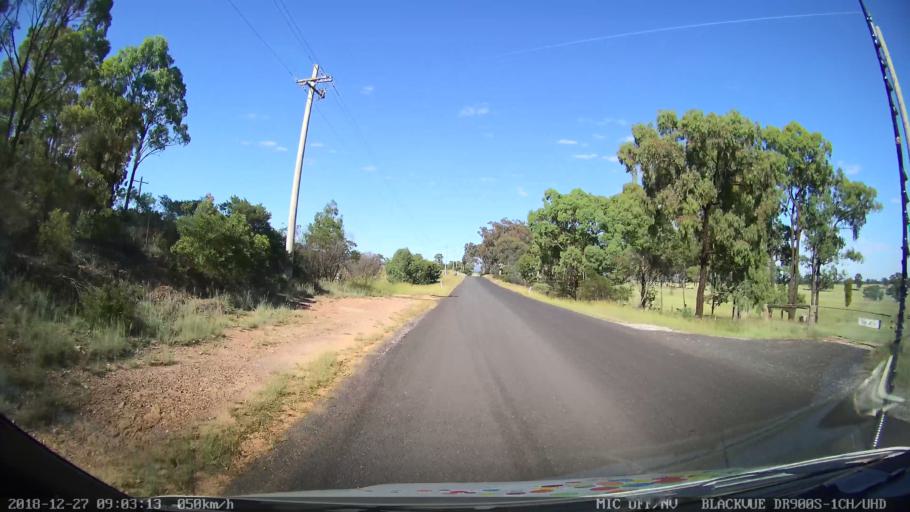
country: AU
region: New South Wales
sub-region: Lithgow
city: Portland
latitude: -33.1043
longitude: 150.2042
